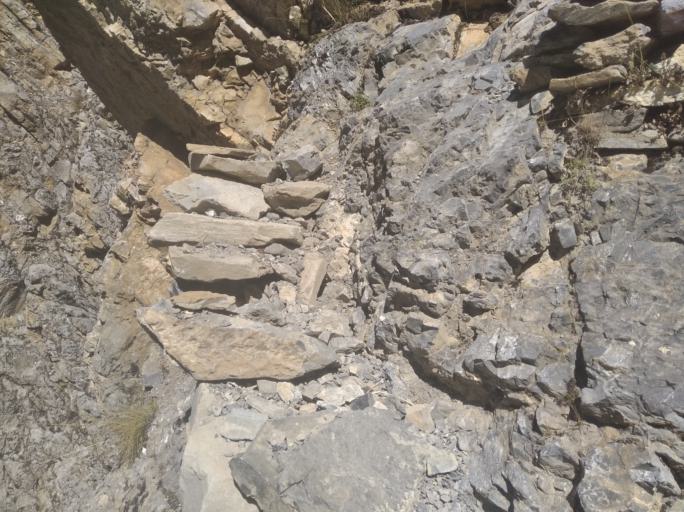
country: NP
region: Western Region
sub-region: Dhawalagiri Zone
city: Jomsom
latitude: 29.0716
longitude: 83.3429
